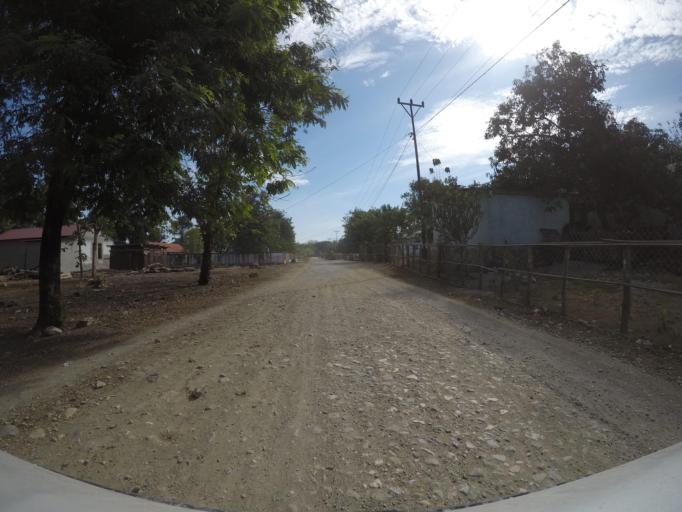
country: TL
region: Bobonaro
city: Maliana
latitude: -8.8820
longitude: 125.2100
